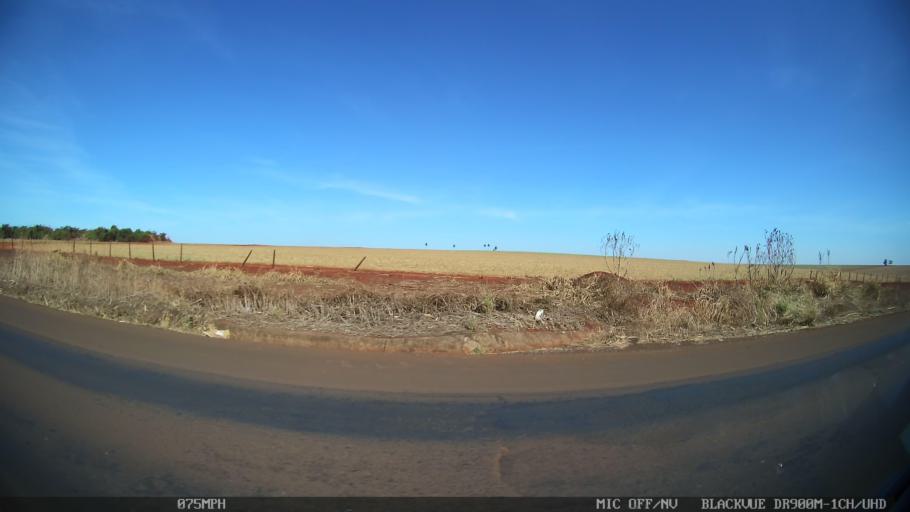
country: BR
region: Sao Paulo
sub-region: Sao Joaquim Da Barra
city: Sao Joaquim da Barra
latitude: -20.5108
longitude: -47.9071
